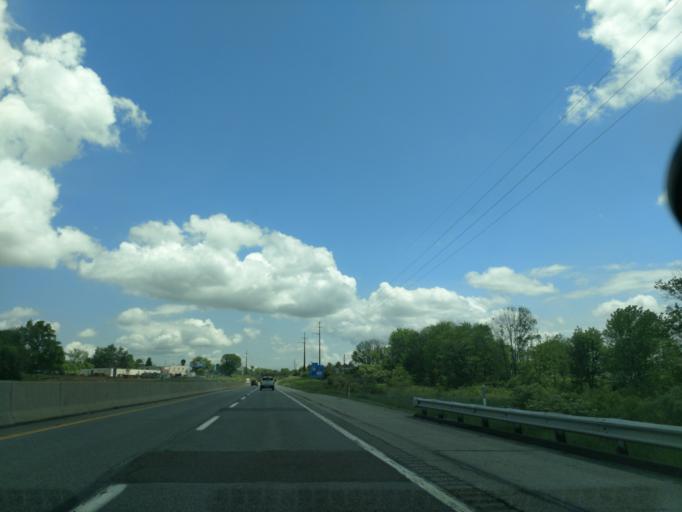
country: US
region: Pennsylvania
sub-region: Lancaster County
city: Swartzville
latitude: 40.2250
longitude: -76.1017
